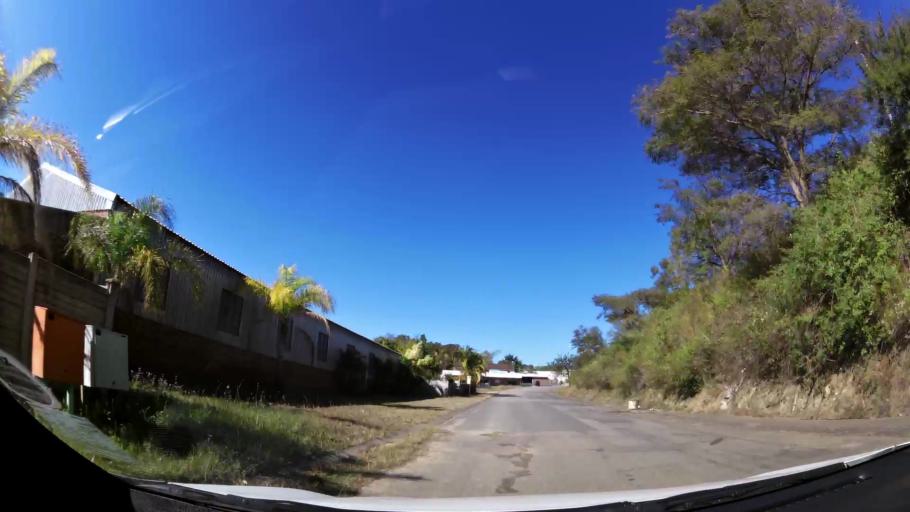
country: ZA
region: Limpopo
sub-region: Mopani District Municipality
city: Tzaneen
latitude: -23.8545
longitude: 30.1679
